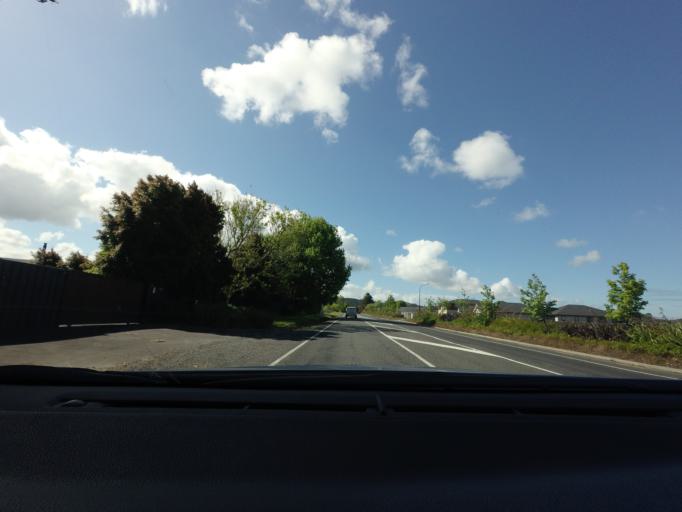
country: NZ
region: Auckland
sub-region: Auckland
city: Rosebank
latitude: -36.7658
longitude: 174.5873
